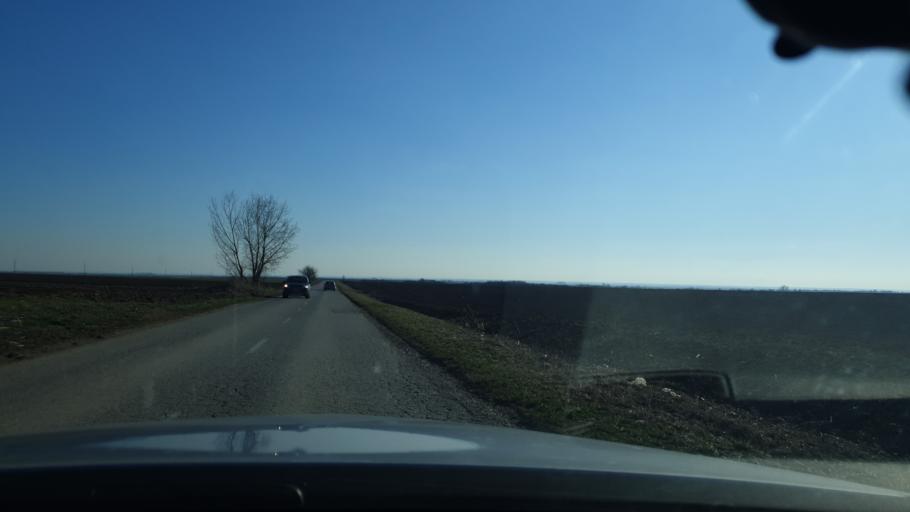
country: RS
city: Vrdnik
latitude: 45.0799
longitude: 19.8080
